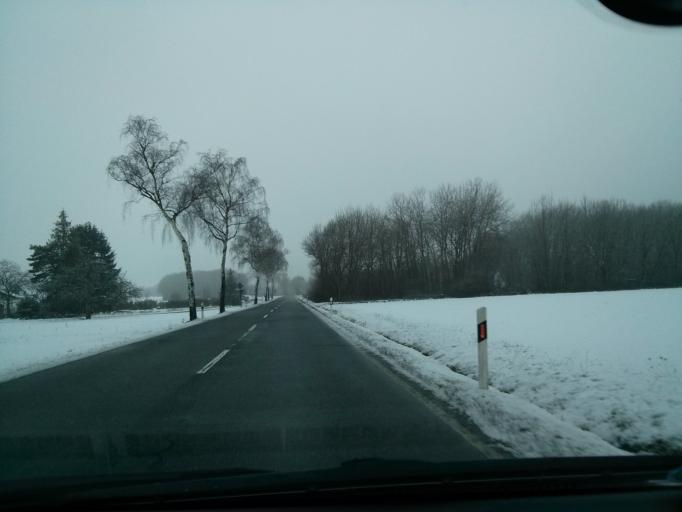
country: DE
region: Rheinland-Pfalz
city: Kirchsahr
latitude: 50.5403
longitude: 6.8786
